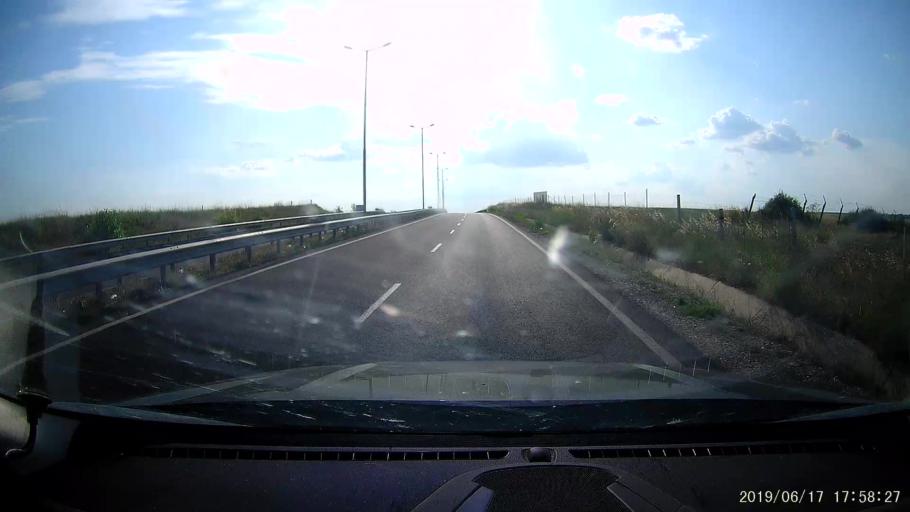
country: BG
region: Khaskovo
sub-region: Obshtina Svilengrad
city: Svilengrad
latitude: 41.7258
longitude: 26.3210
